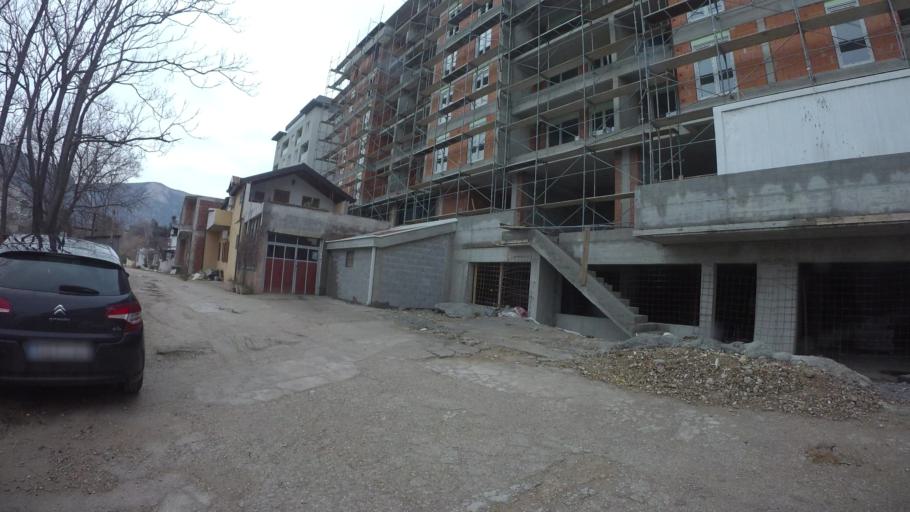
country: BA
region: Federation of Bosnia and Herzegovina
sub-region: Hercegovacko-Bosanski Kanton
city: Mostar
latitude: 43.3495
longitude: 17.8120
